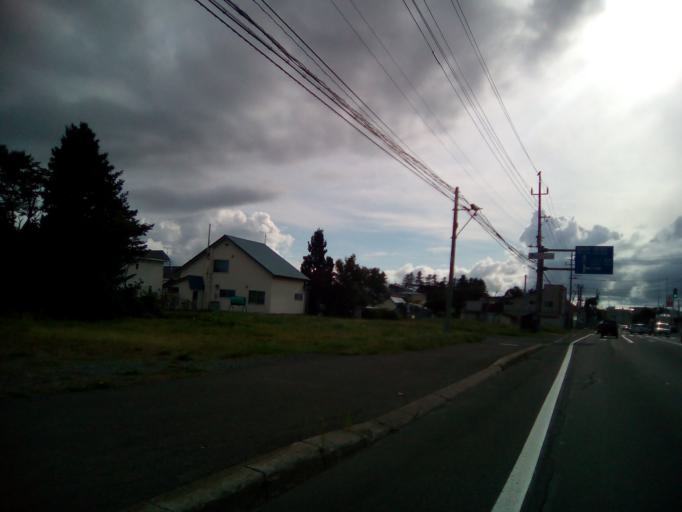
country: JP
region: Hokkaido
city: Niseko Town
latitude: 42.7397
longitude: 140.8816
